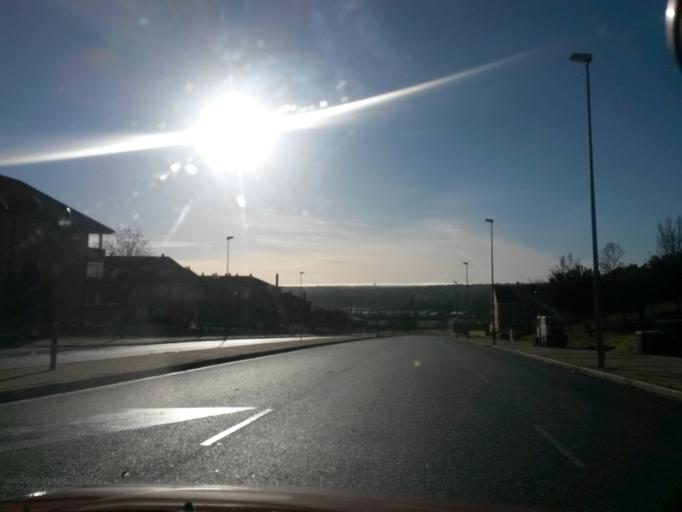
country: ES
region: Castille and Leon
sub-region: Provincia de Salamanca
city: Salamanca
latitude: 40.9665
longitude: -5.6867
